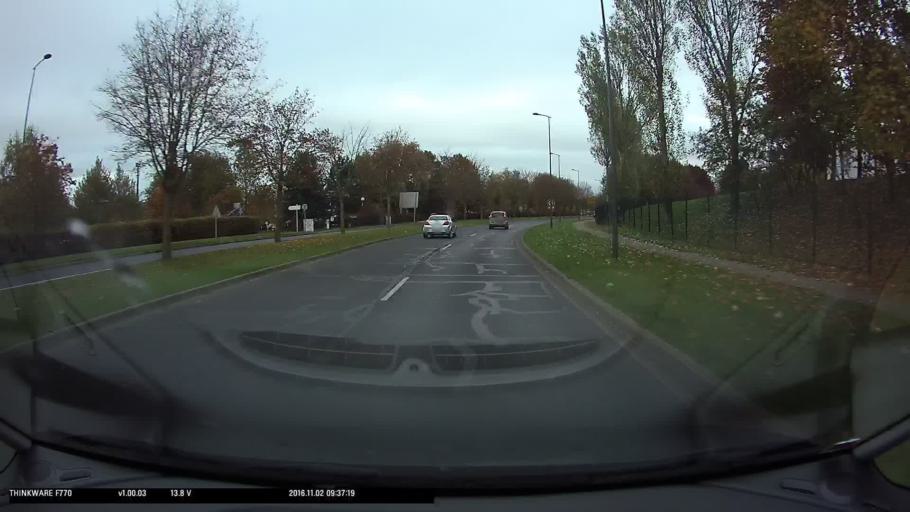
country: FR
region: Ile-de-France
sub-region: Departement du Val-d'Oise
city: Vaureal
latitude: 49.0548
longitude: 2.0249
